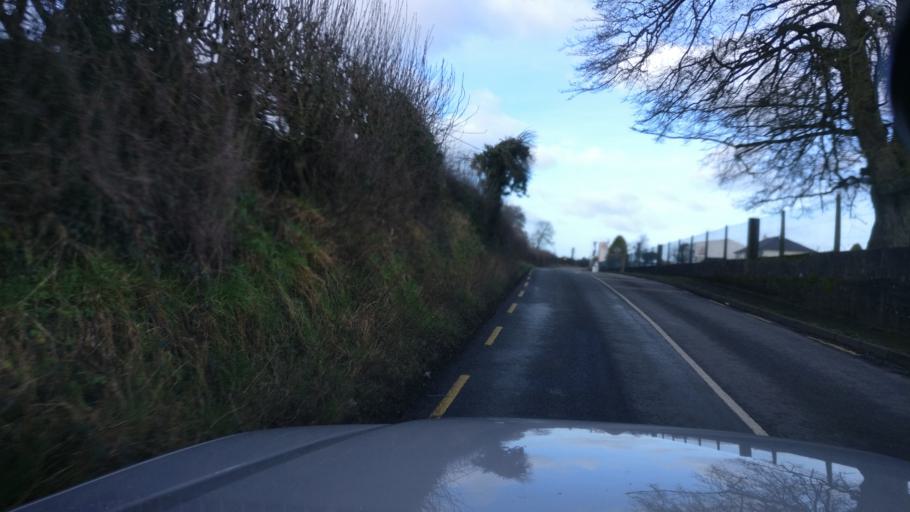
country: IE
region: Leinster
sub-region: Kilkenny
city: Castlecomer
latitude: 52.8097
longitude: -7.2112
